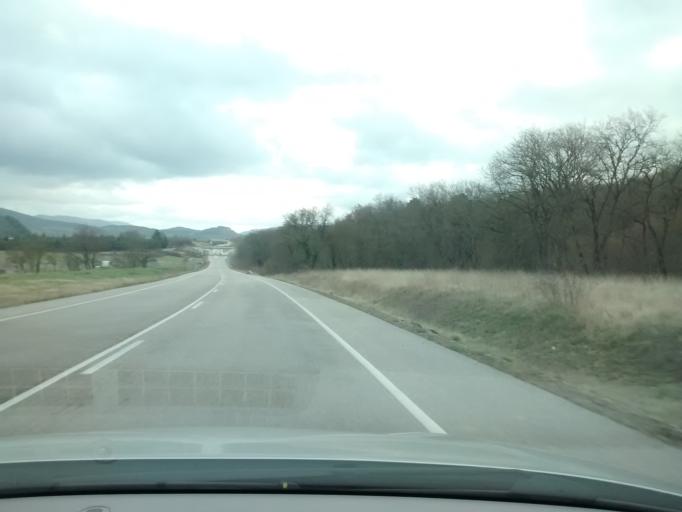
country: ES
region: Castille and Leon
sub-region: Provincia de Burgos
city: Villasana de Mena
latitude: 43.0964
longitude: -3.2772
